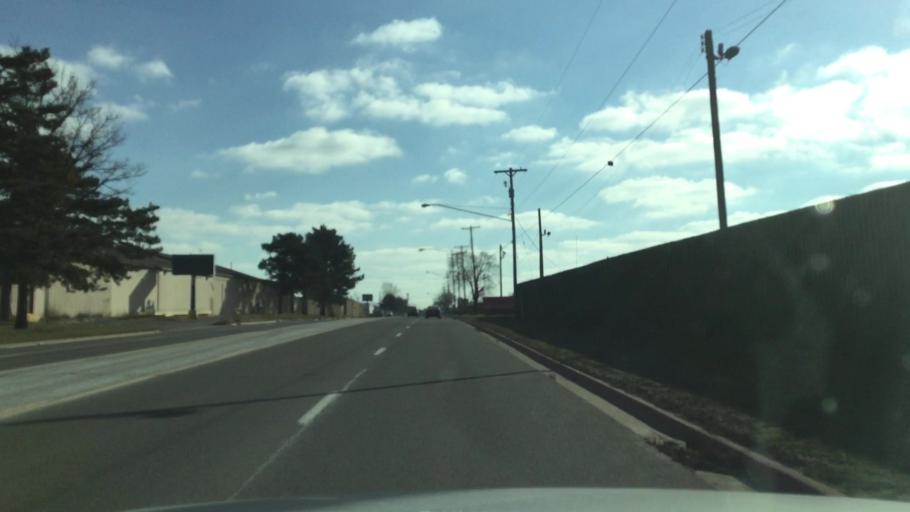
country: US
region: Michigan
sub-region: Genesee County
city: Flint
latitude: 43.0492
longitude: -83.6619
